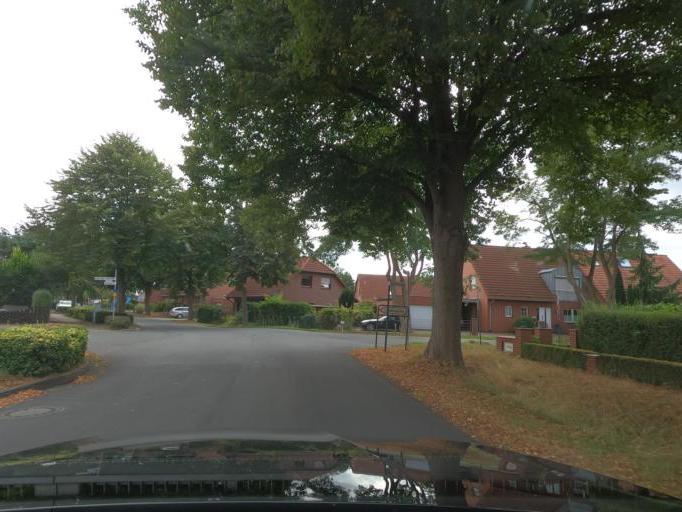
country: DE
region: Lower Saxony
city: Isernhagen Farster Bauerschaft
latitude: 52.4473
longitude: 9.8946
